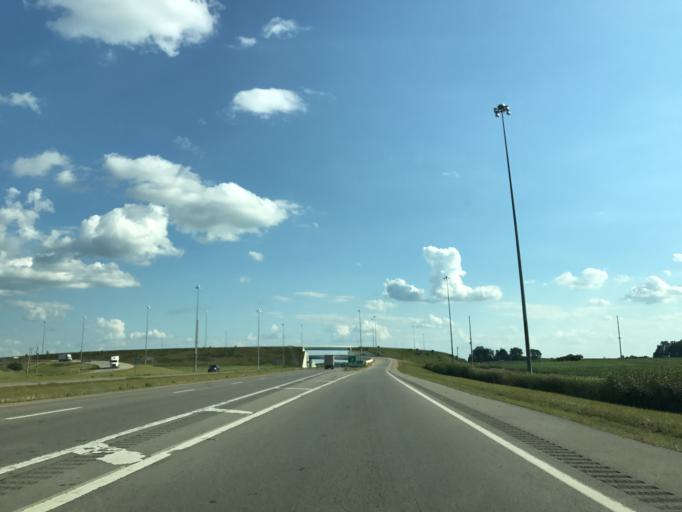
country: US
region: Ohio
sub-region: Wyandot County
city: Upper Sandusky
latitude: 40.8169
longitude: -83.2368
